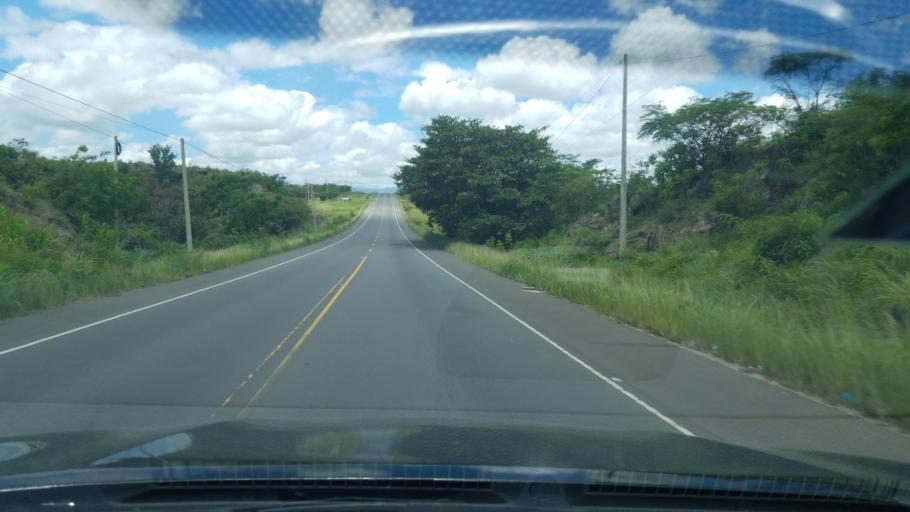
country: HN
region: Francisco Morazan
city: Cofradia
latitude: 14.3005
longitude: -87.2347
